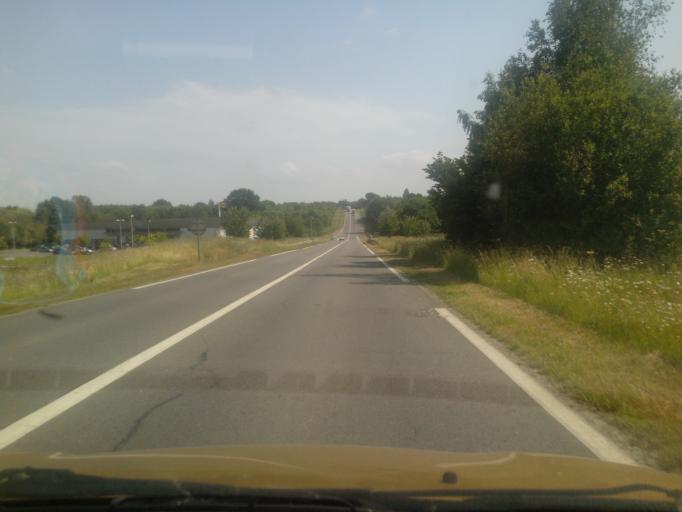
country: FR
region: Brittany
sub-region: Departement d'Ille-et-Vilaine
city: Melesse
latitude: 48.2139
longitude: -1.7013
